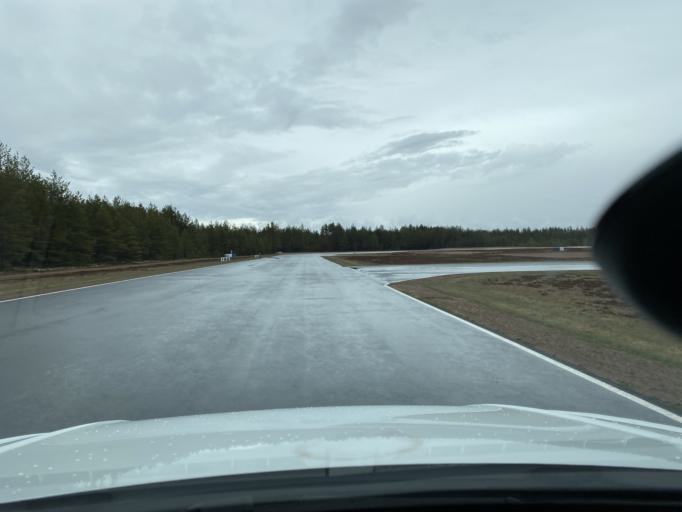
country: FI
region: Satakunta
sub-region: Pori
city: Vampula
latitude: 60.9779
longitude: 22.6628
